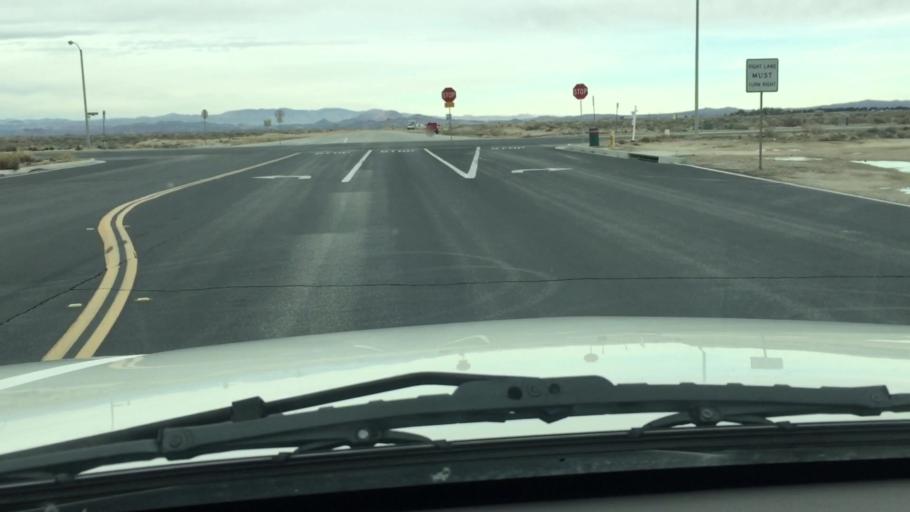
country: US
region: California
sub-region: Los Angeles County
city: Lancaster
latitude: 34.7326
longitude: -118.1840
